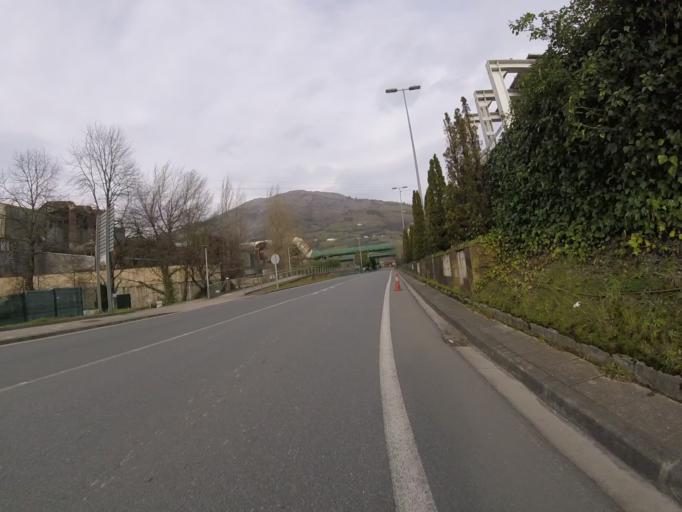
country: ES
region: Basque Country
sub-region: Provincia de Guipuzcoa
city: Azpeitia
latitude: 43.1806
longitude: -2.2597
